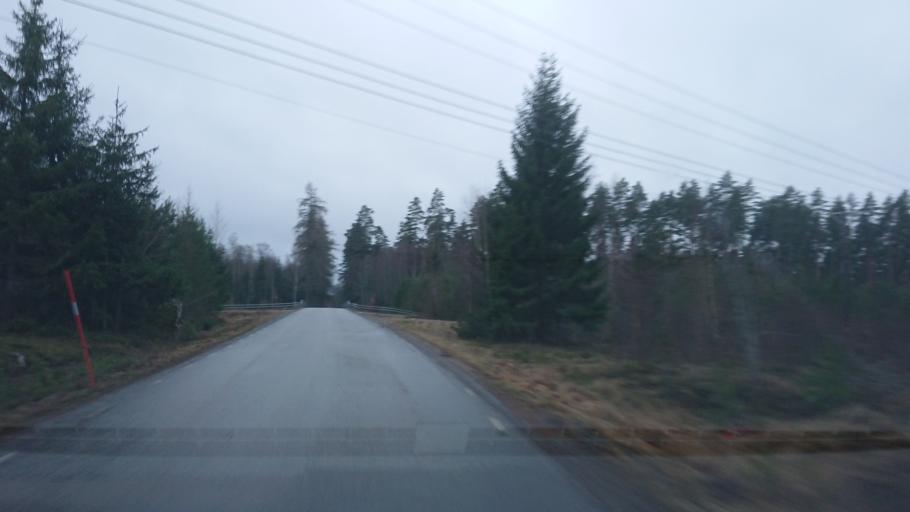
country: SE
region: Uppsala
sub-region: Osthammars Kommun
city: Bjorklinge
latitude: 60.0194
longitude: 17.5836
